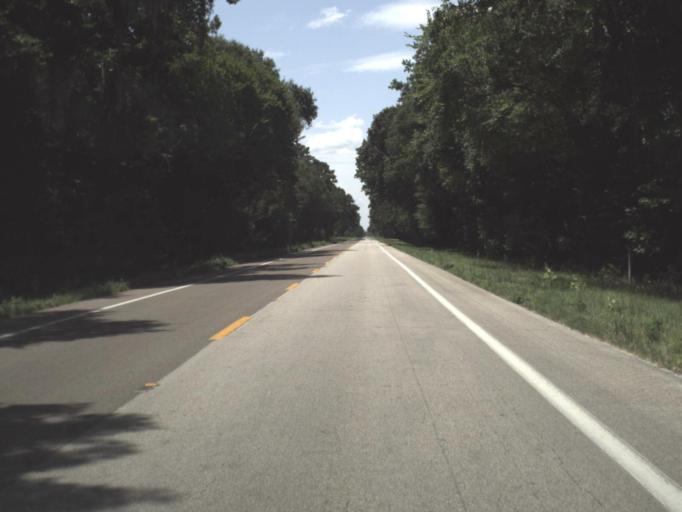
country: US
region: Florida
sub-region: Gilchrist County
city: Trenton
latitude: 29.6362
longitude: -82.8286
